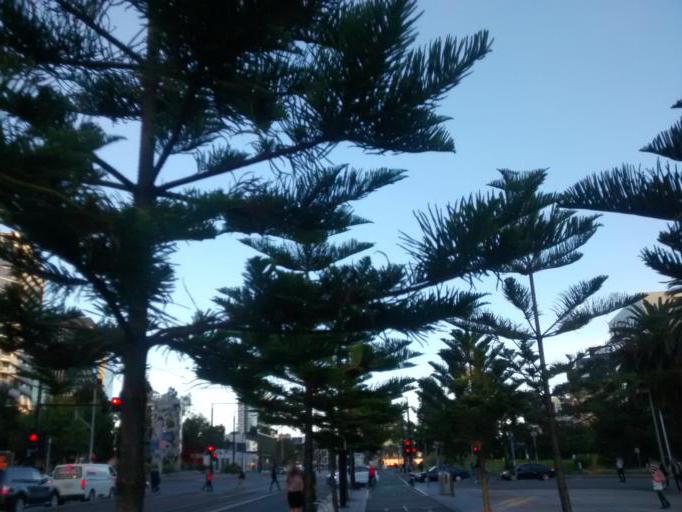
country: AU
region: Victoria
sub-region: Melbourne
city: Docklands
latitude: -37.8185
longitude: 144.9464
